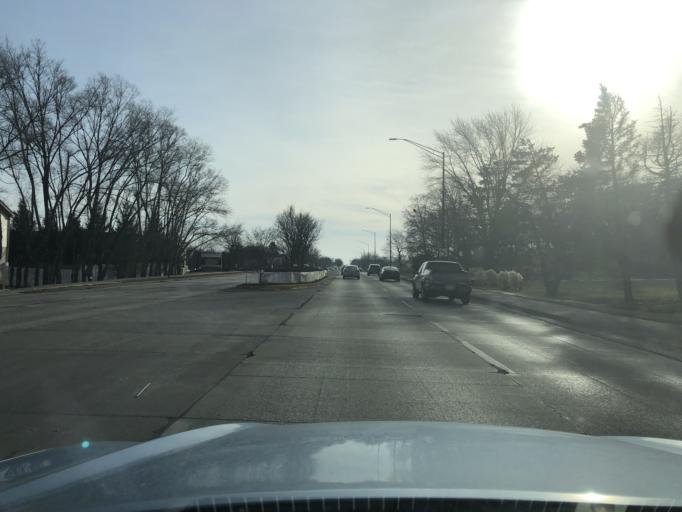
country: US
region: Illinois
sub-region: Cook County
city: Schaumburg
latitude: 42.0125
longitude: -88.0801
